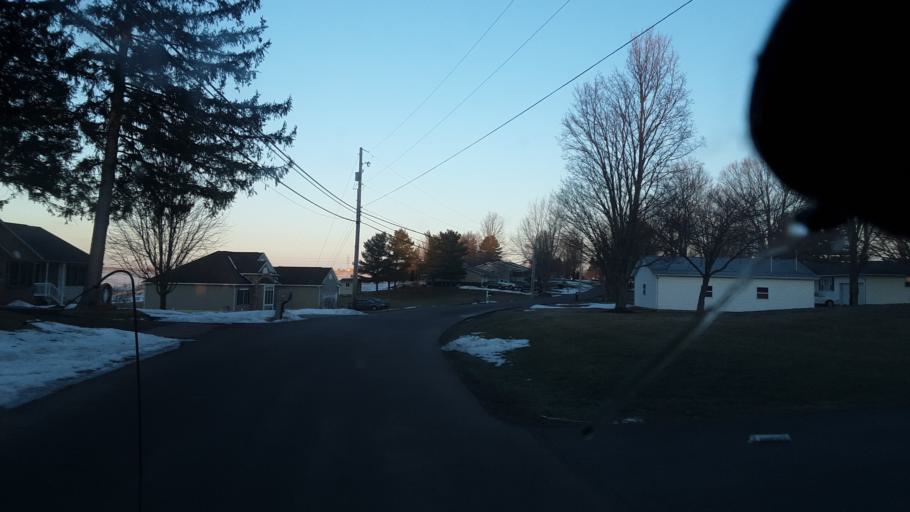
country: US
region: Ohio
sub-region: Perry County
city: Somerset
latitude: 39.8121
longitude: -82.3098
